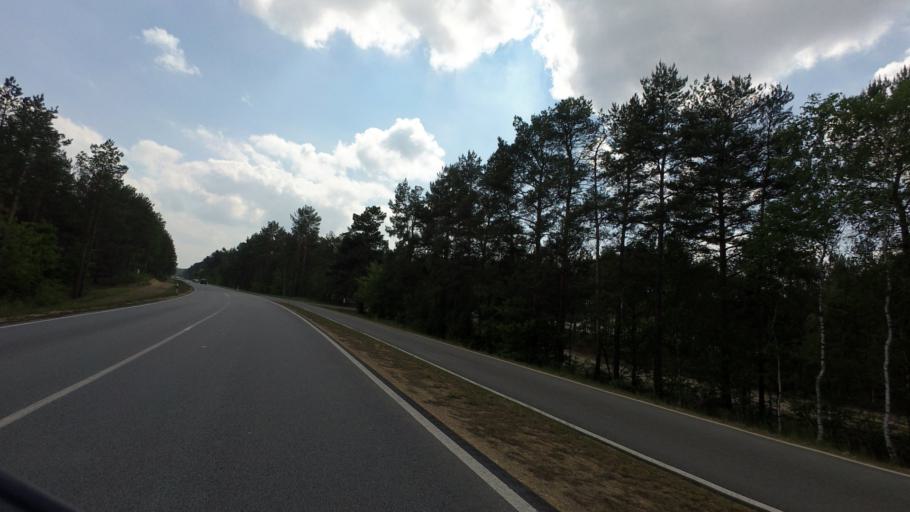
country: DE
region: Saxony
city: Rietschen
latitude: 51.4337
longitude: 14.7841
